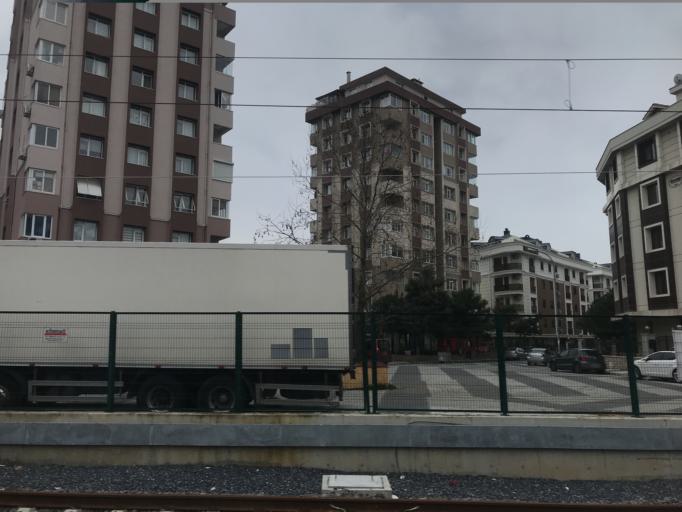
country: TR
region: Istanbul
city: Maltepe
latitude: 40.9159
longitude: 29.1448
